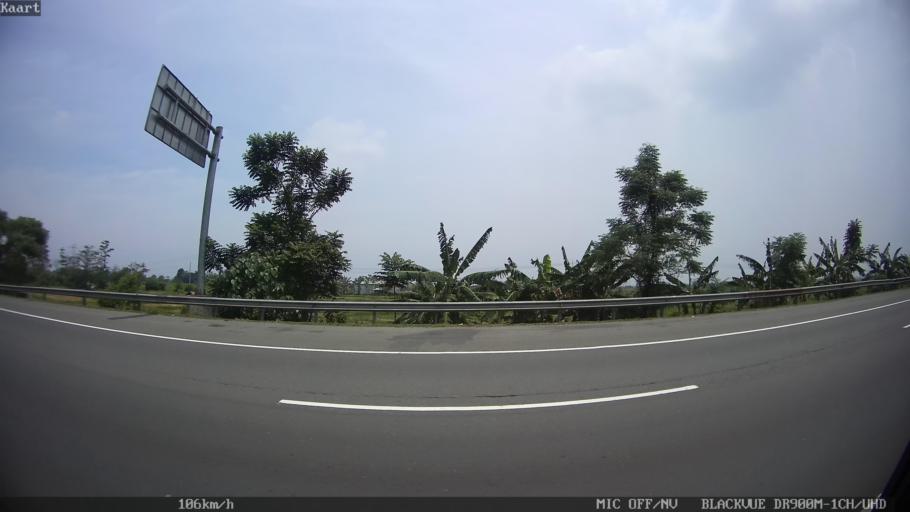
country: ID
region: West Java
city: Kresek
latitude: -6.1771
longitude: 106.3582
